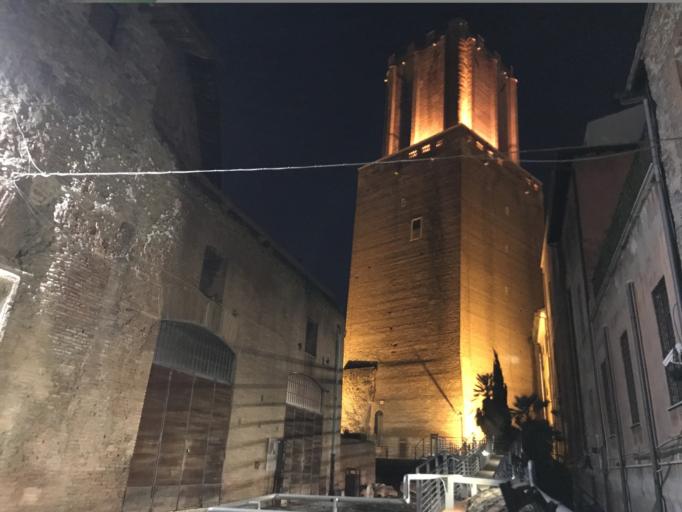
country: IT
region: Latium
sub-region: Citta metropolitana di Roma Capitale
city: Rome
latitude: 41.8954
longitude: 12.4866
